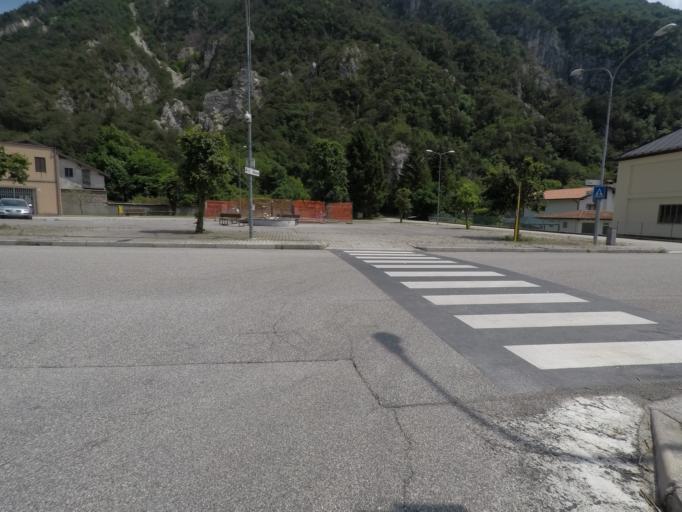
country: IT
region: Friuli Venezia Giulia
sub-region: Provincia di Udine
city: Amaro
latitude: 46.3734
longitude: 13.1347
